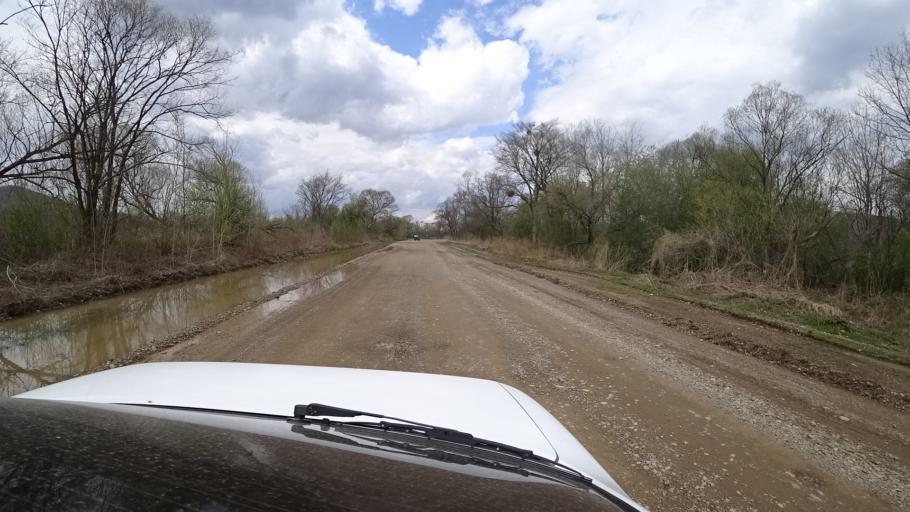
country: RU
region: Primorskiy
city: Novopokrovka
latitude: 45.6104
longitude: 134.2754
